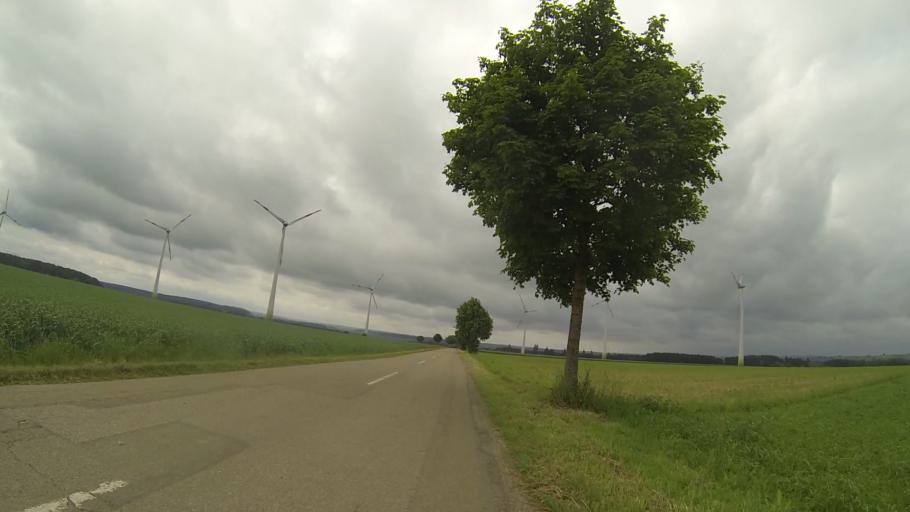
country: DE
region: Baden-Wuerttemberg
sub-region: Regierungsbezirk Stuttgart
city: Bartholoma
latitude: 48.6978
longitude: 9.9997
